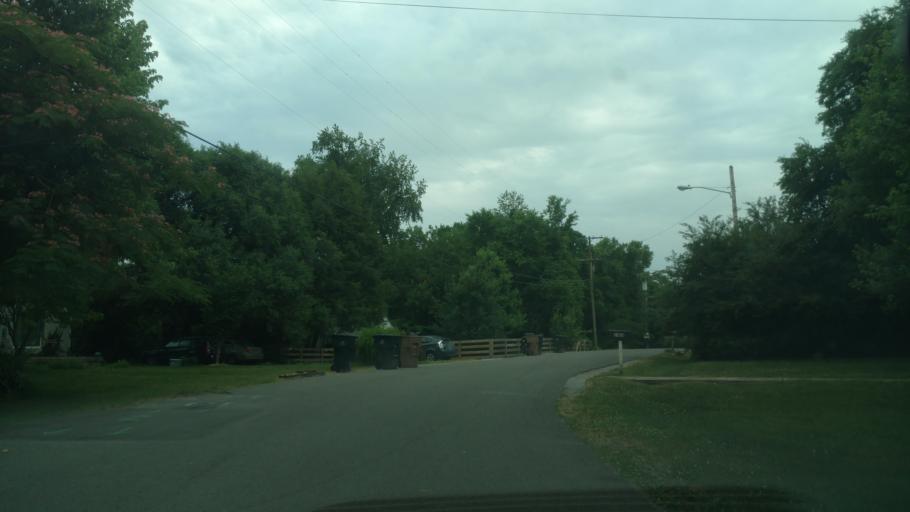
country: US
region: Tennessee
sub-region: Davidson County
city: Lakewood
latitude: 36.2161
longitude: -86.7097
